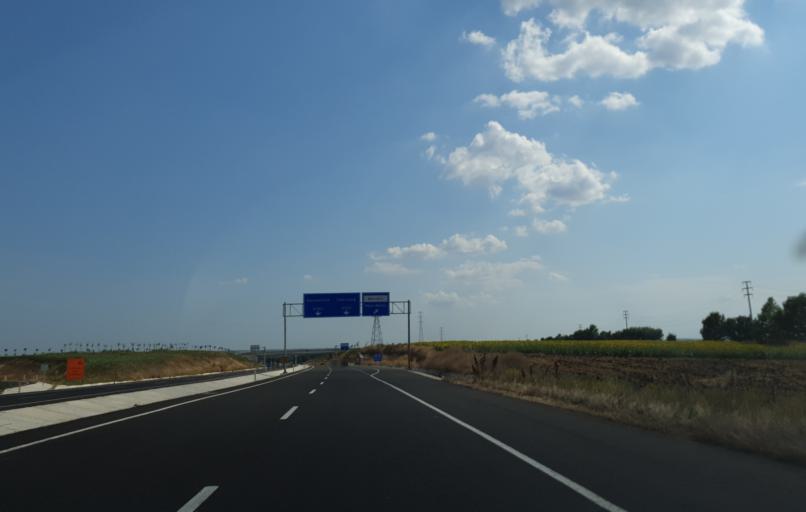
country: TR
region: Tekirdag
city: Muratli
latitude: 41.2293
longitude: 27.5327
